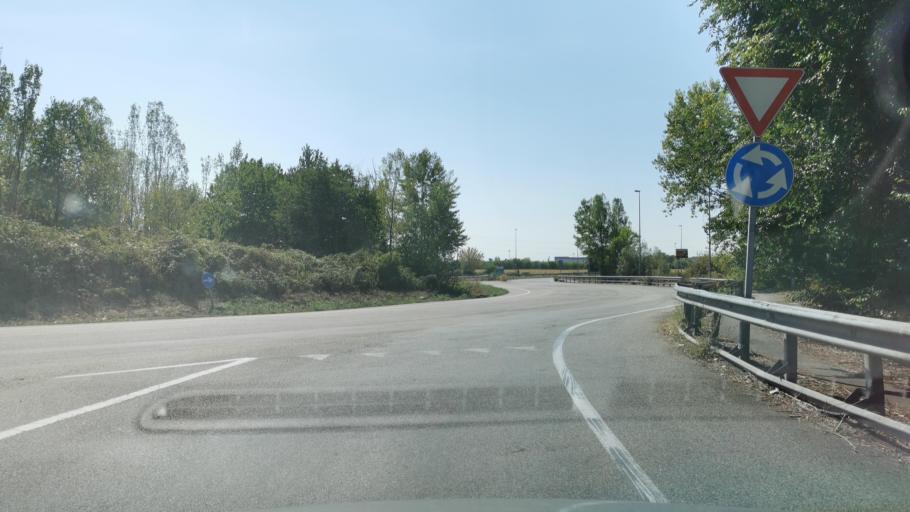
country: IT
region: Piedmont
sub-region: Provincia di Torino
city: Grugliasco
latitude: 45.0538
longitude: 7.5665
